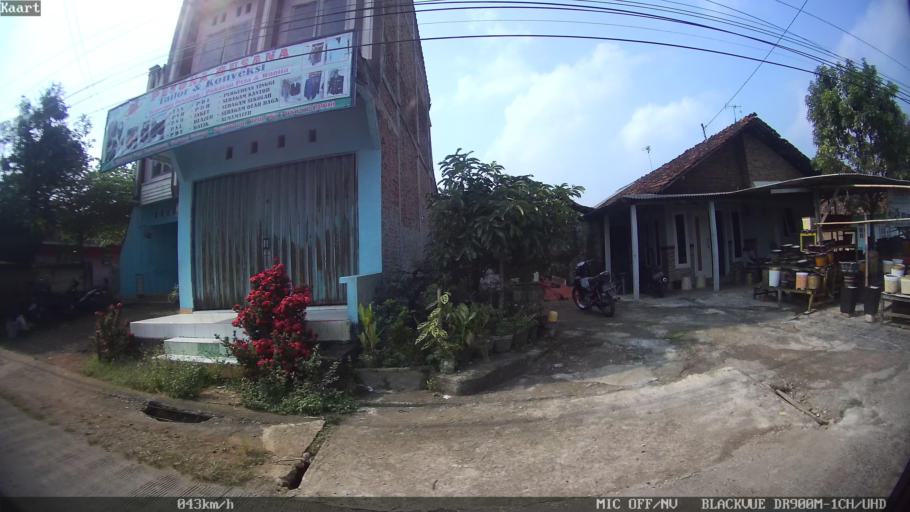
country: ID
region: Lampung
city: Gedongtataan
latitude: -5.3795
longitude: 105.1216
